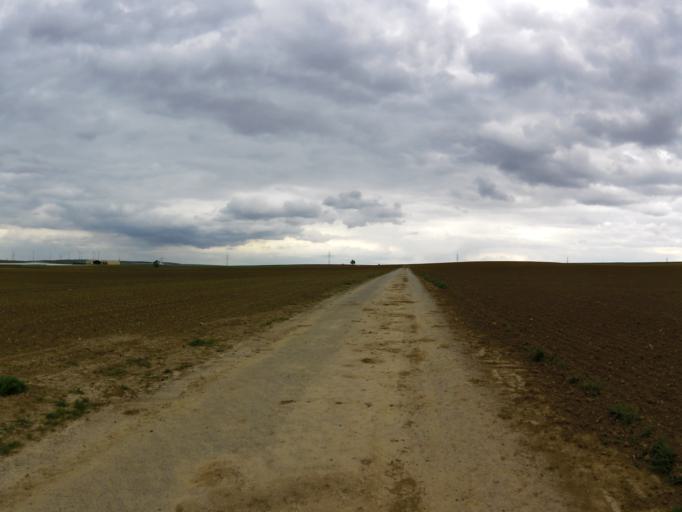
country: DE
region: Bavaria
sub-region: Regierungsbezirk Unterfranken
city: Oberpleichfeld
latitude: 49.8564
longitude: 10.0710
